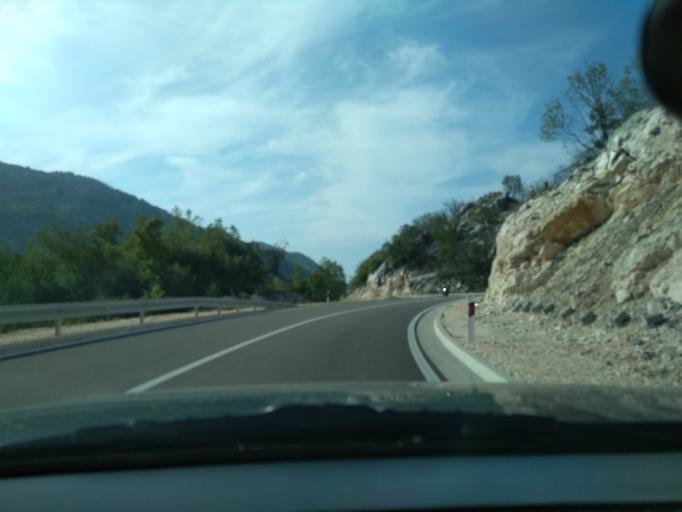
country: ME
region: Cetinje
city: Cetinje
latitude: 42.4269
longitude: 18.8670
